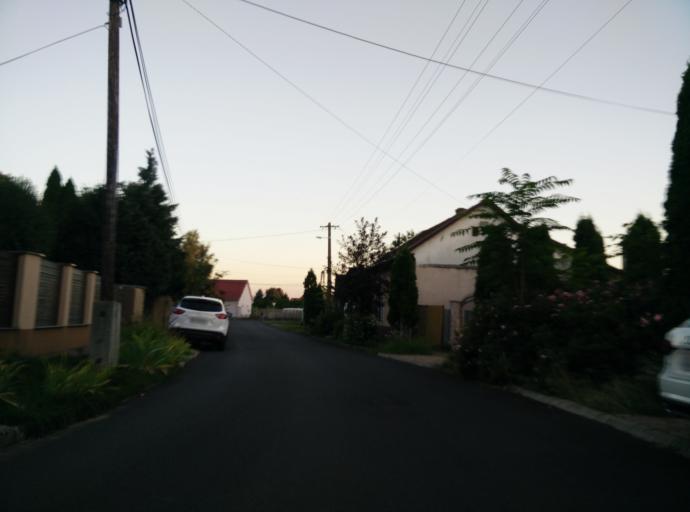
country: HU
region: Heves
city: Hatvan
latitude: 47.6650
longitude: 19.6948
